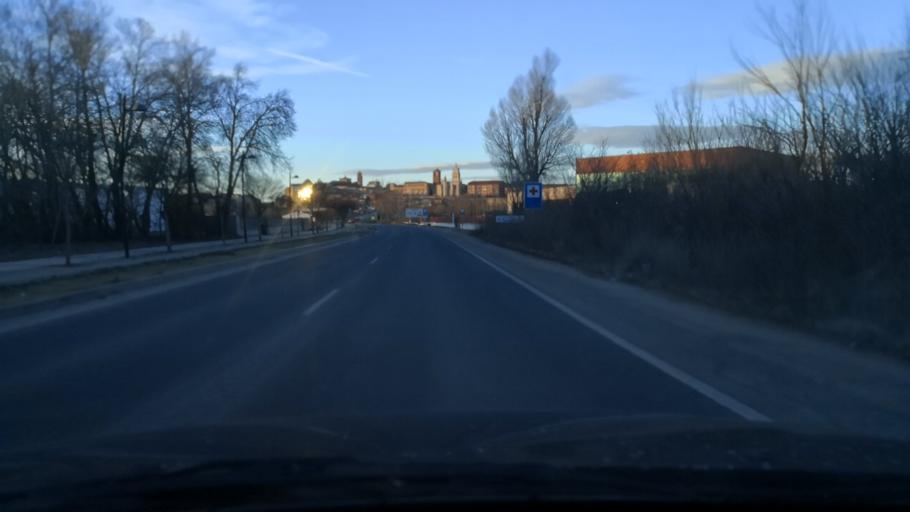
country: ES
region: Castille and Leon
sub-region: Provincia de Valladolid
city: Tordesillas
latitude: 41.4932
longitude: -4.9981
